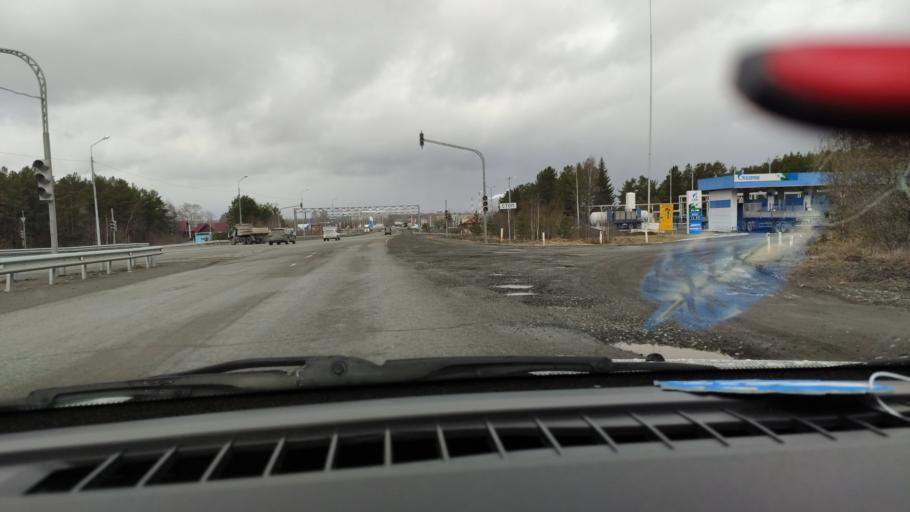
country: RU
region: Sverdlovsk
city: Talitsa
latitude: 56.8761
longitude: 60.0305
